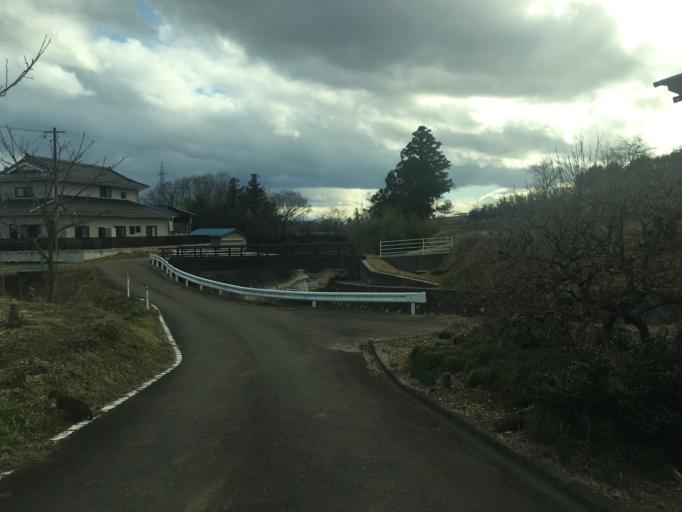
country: JP
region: Fukushima
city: Yanagawamachi-saiwaicho
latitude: 37.8934
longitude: 140.5813
